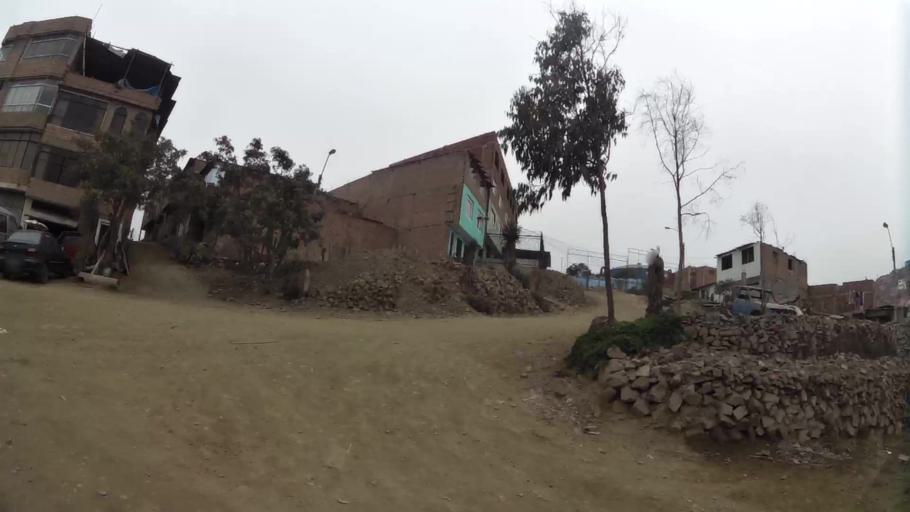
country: PE
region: Lima
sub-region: Lima
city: Surco
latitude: -12.1637
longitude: -76.9571
